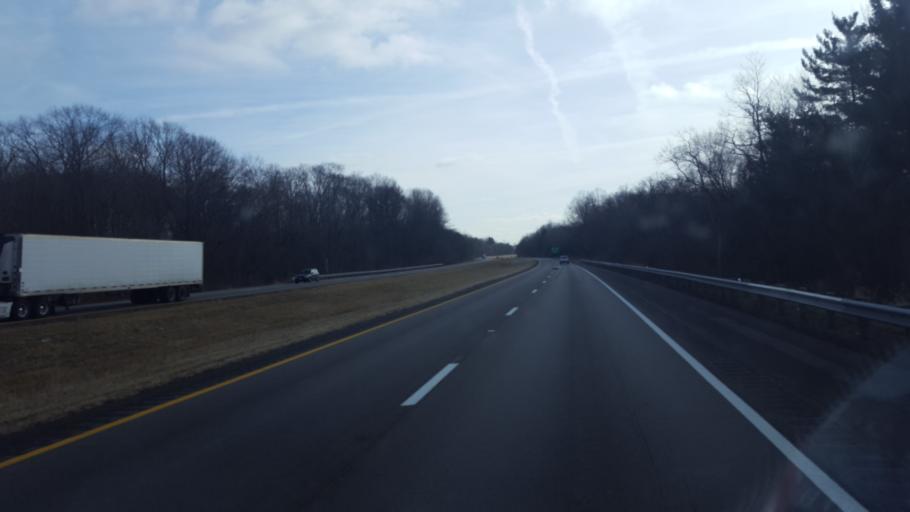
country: US
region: Ohio
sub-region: Stark County
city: Brewster
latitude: 40.7756
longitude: -81.5971
